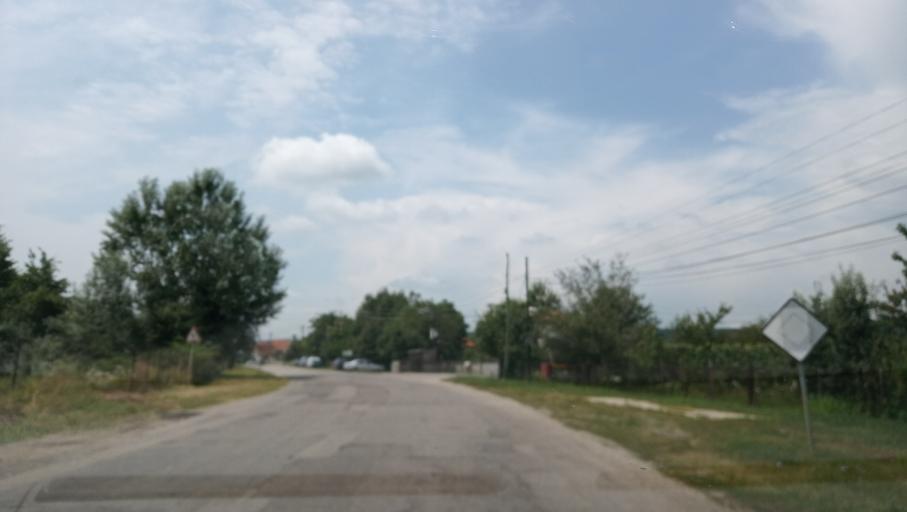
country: RO
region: Gorj
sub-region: Comuna Turcinesti
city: Turcinesti
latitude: 45.1097
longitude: 23.3186
